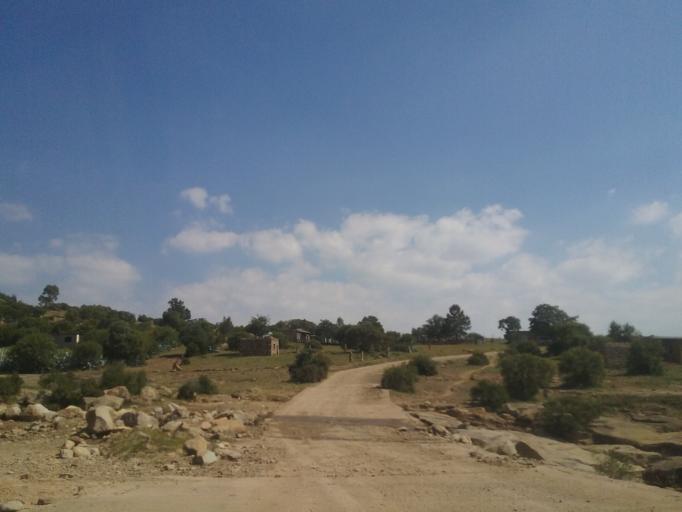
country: LS
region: Maseru
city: Maseru
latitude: -29.4000
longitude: 27.4543
